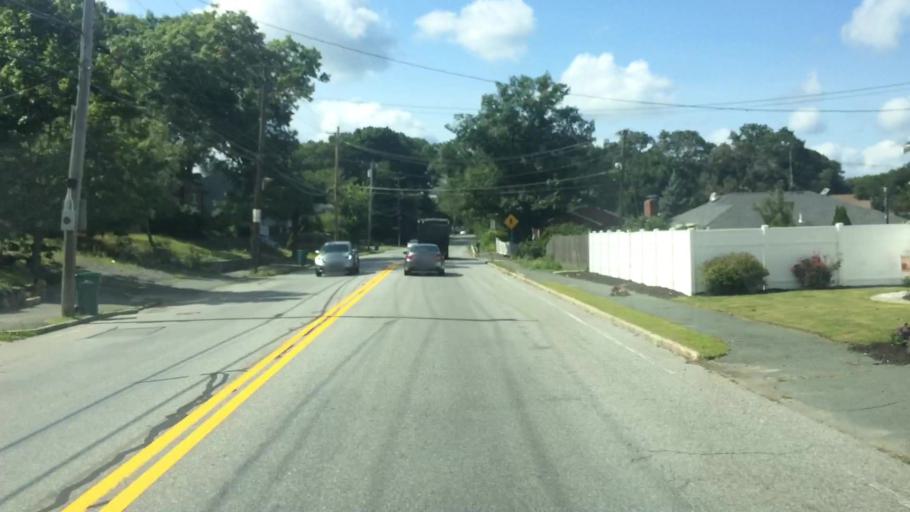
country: US
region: Massachusetts
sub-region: Essex County
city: South Peabody
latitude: 42.4998
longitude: -70.9753
